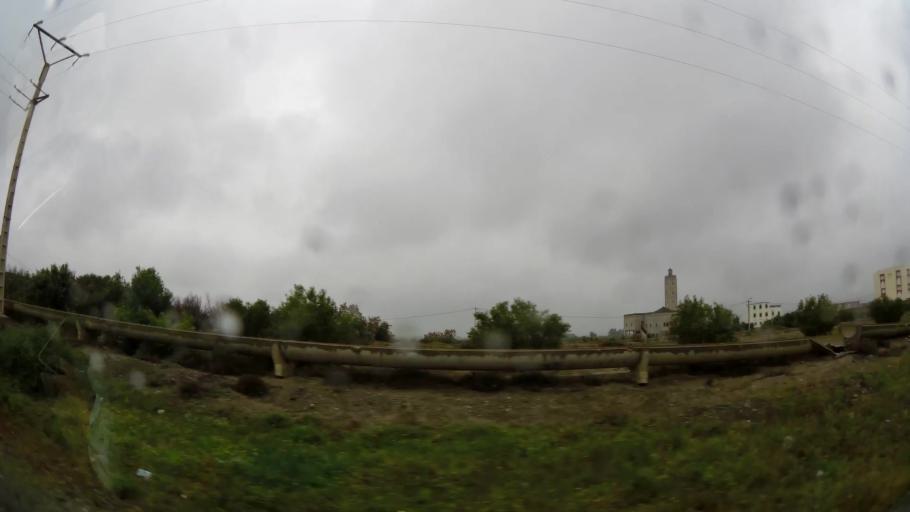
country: MA
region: Taza-Al Hoceima-Taounate
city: Imzourene
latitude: 35.1409
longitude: -3.8028
